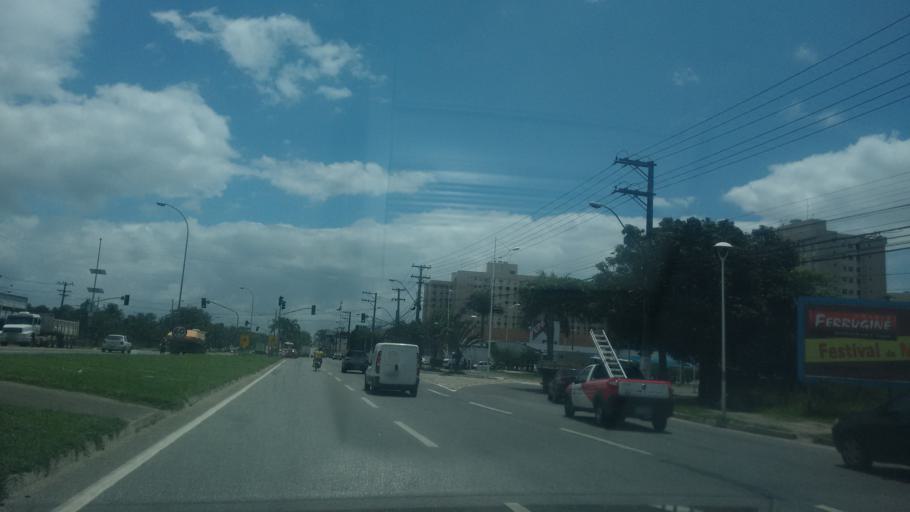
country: BR
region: Espirito Santo
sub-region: Serra
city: Serra
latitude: -20.1944
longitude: -40.2685
